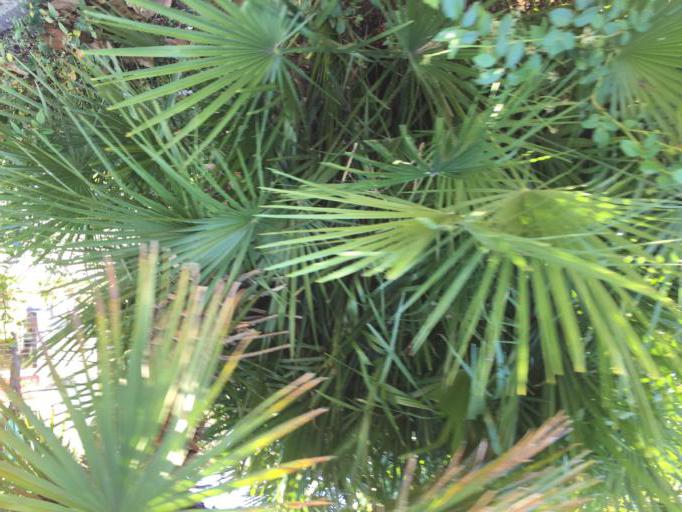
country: IT
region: Latium
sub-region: Provincia di Latina
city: Gaeta
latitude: 41.2155
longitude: 13.5715
